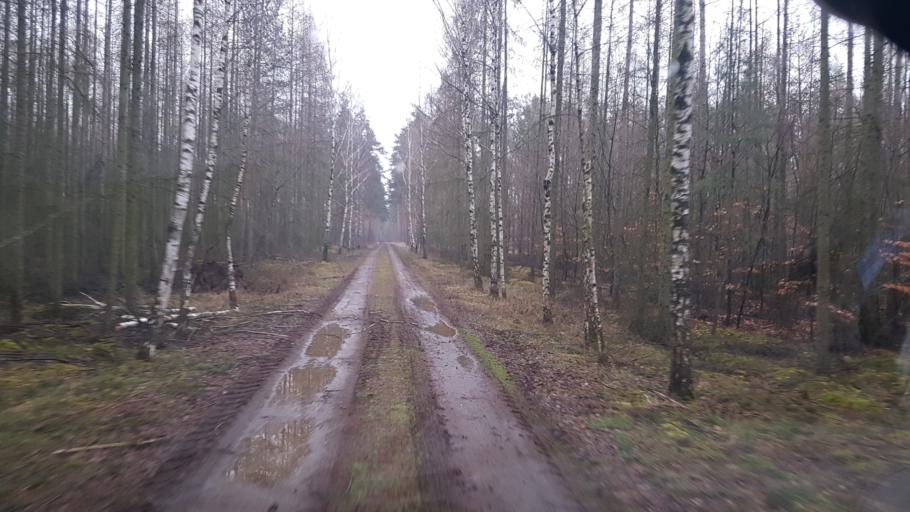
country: DE
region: Brandenburg
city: Muhlberg
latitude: 51.4909
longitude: 13.2897
